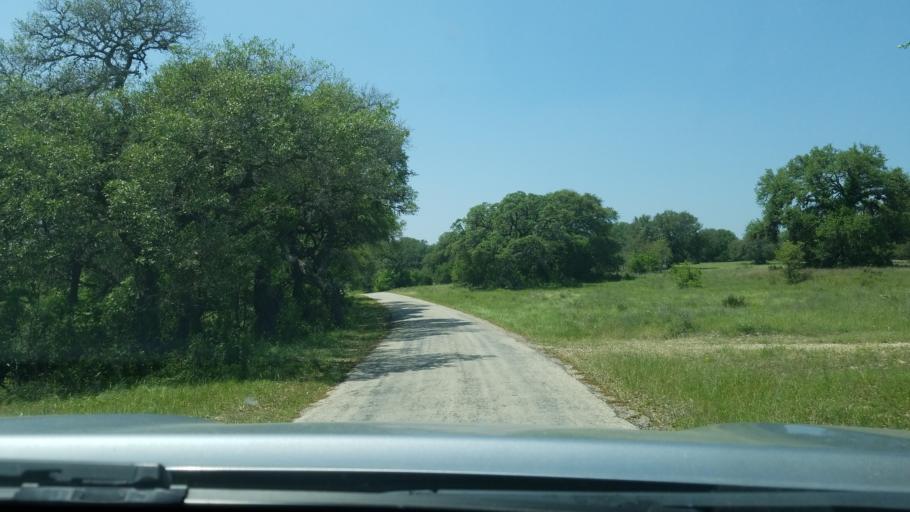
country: US
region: Texas
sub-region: Blanco County
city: Blanco
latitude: 30.0164
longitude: -98.4523
